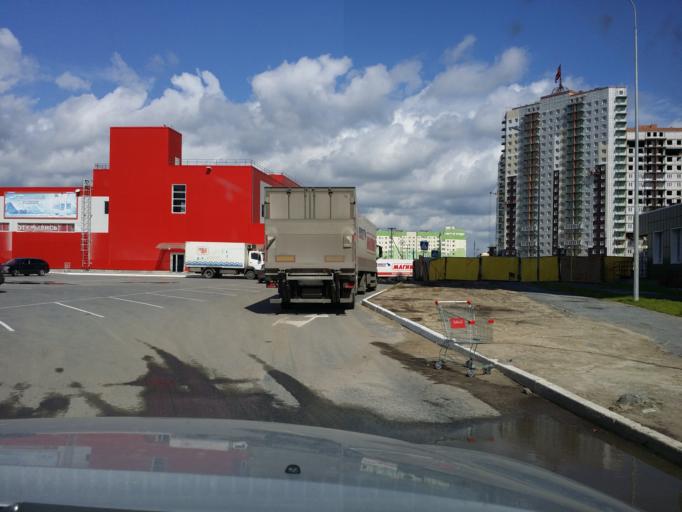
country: RU
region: Khanty-Mansiyskiy Avtonomnyy Okrug
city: Nizhnevartovsk
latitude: 60.9283
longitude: 76.6091
